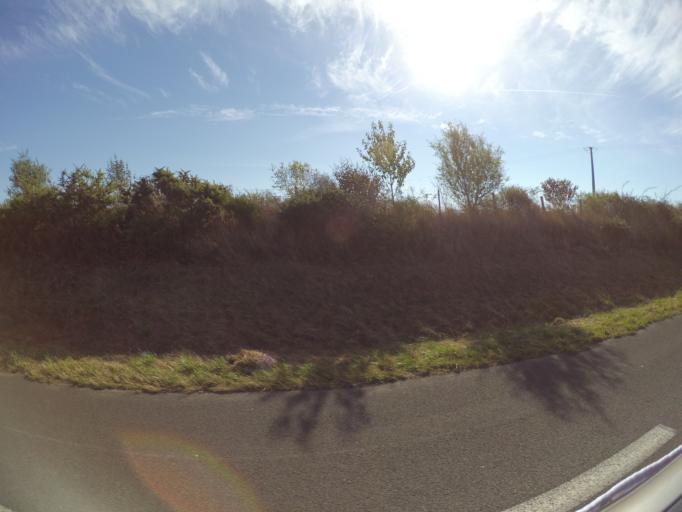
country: FR
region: Pays de la Loire
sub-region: Departement de Maine-et-Loire
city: Vezins
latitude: 47.1221
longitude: -0.7259
